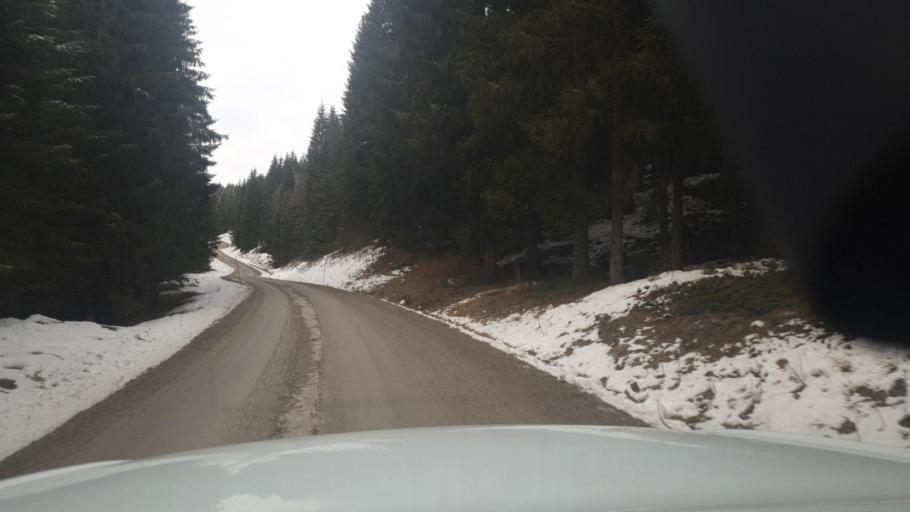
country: SE
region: Vaermland
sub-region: Sunne Kommun
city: Sunne
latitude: 59.8601
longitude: 12.8809
